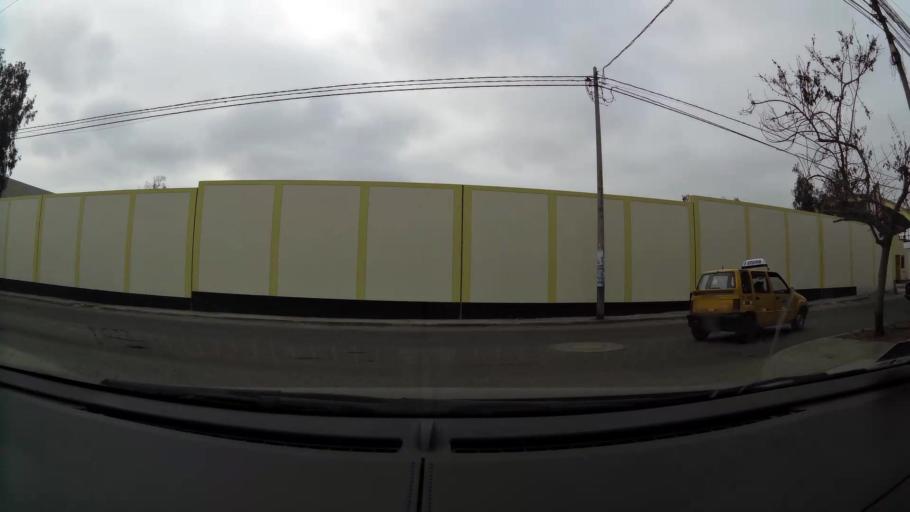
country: PE
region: La Libertad
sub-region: Provincia de Trujillo
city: Trujillo
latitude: -8.1035
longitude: -79.0272
